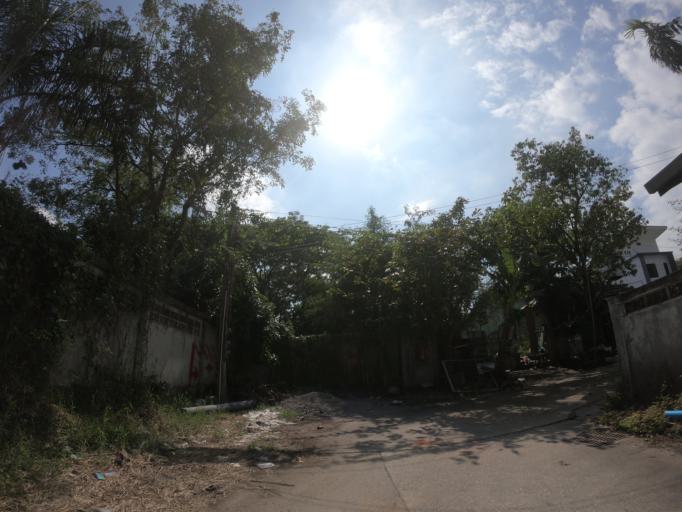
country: TH
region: Chiang Mai
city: Chiang Mai
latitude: 18.7718
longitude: 98.9875
